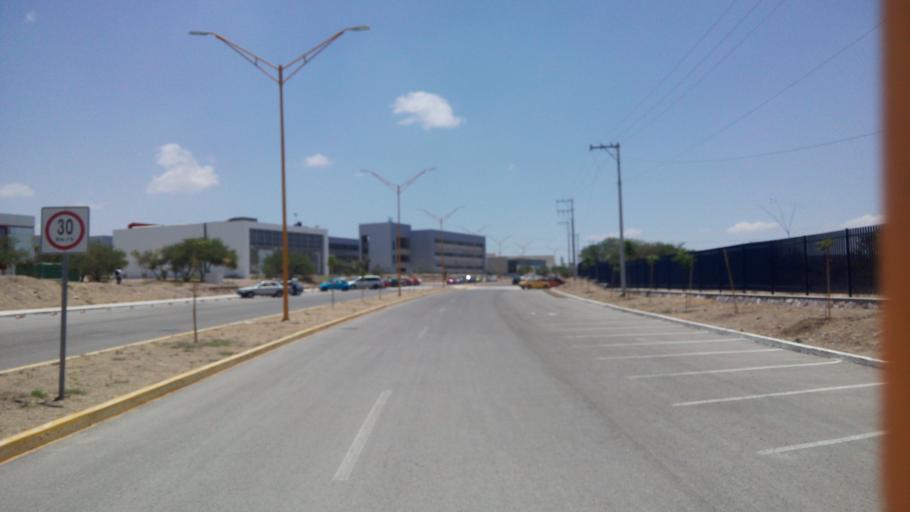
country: MX
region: Aguascalientes
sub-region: Aguascalientes
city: San Sebastian [Fraccionamiento]
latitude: 21.7918
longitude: -102.2922
